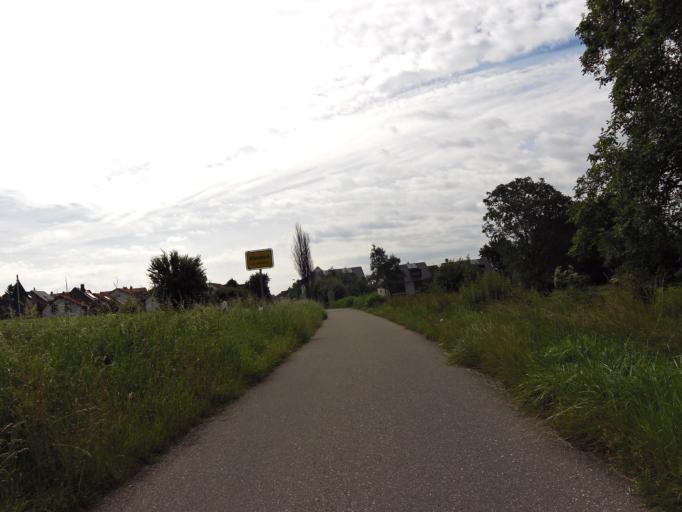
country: DE
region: Baden-Wuerttemberg
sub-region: Freiburg Region
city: Allensbach
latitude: 47.7221
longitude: 9.0495
